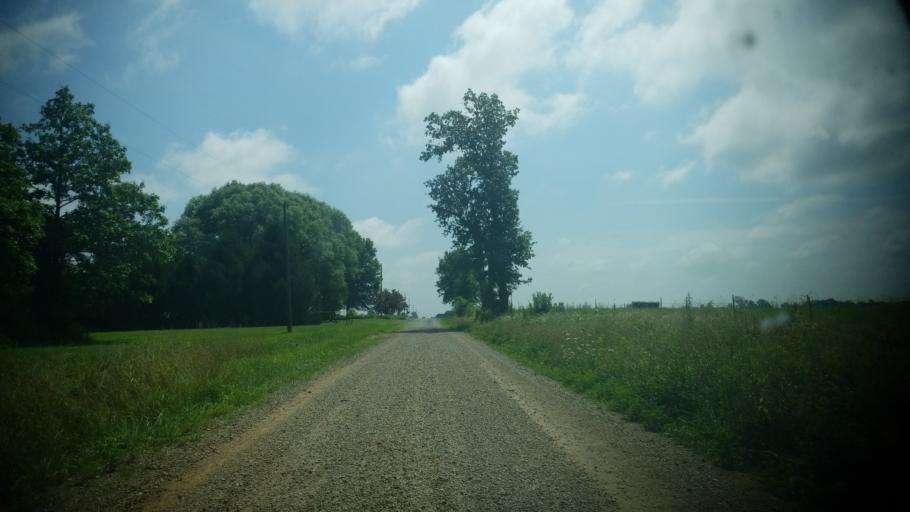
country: US
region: Illinois
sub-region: Wayne County
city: Fairfield
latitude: 38.5300
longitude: -88.3907
